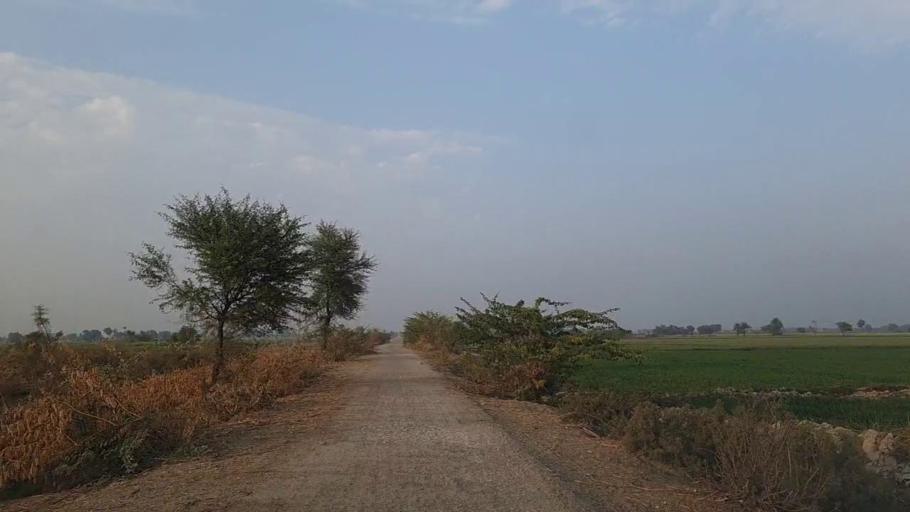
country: PK
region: Sindh
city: Jam Sahib
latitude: 26.3047
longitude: 68.6088
